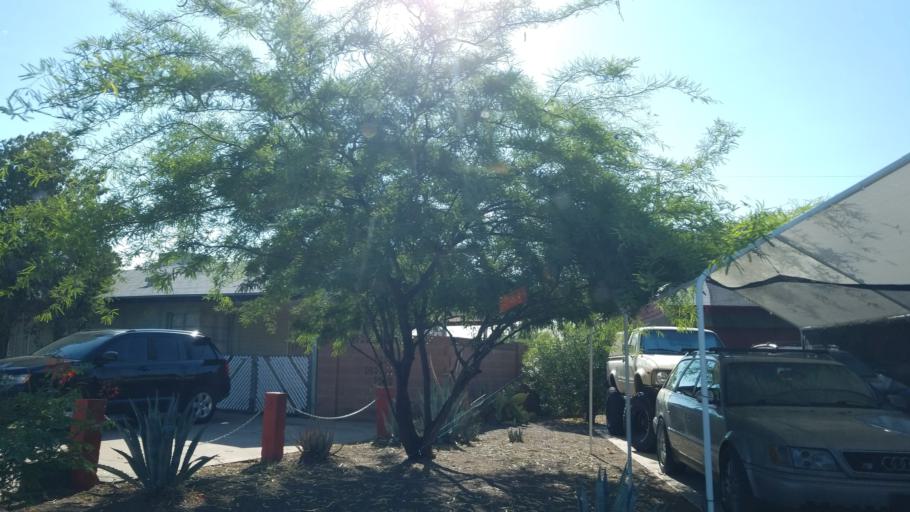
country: US
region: Arizona
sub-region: Maricopa County
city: Phoenix
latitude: 33.4985
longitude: -112.0604
